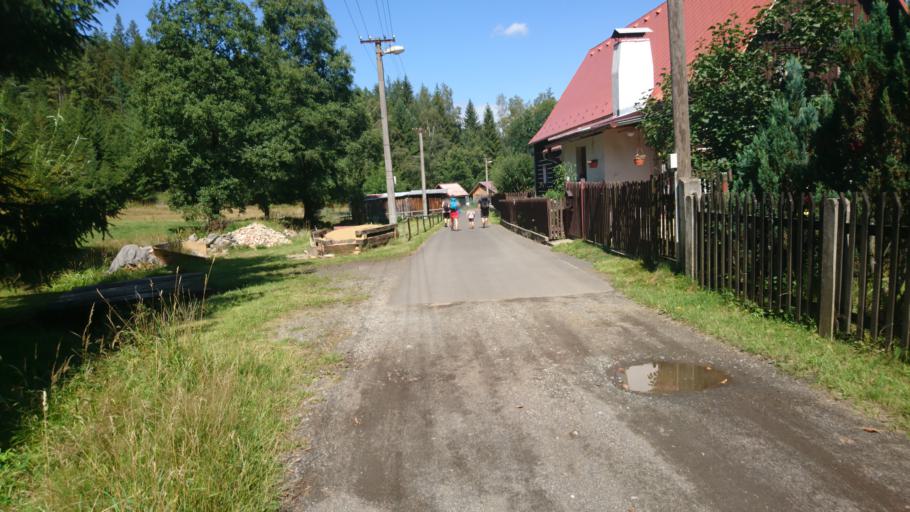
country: CZ
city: Kamenicky Senov
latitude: 50.8090
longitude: 14.4980
